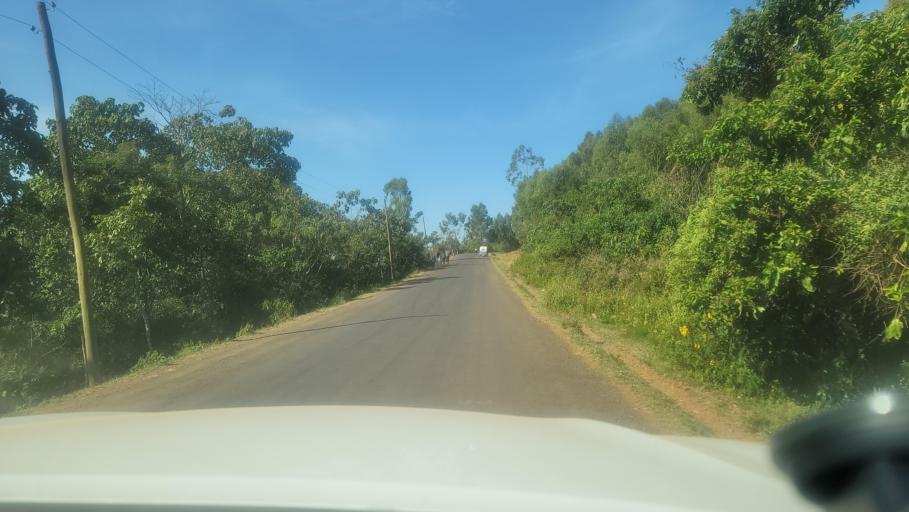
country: ET
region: Oromiya
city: Agaro
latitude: 7.7960
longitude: 36.4840
